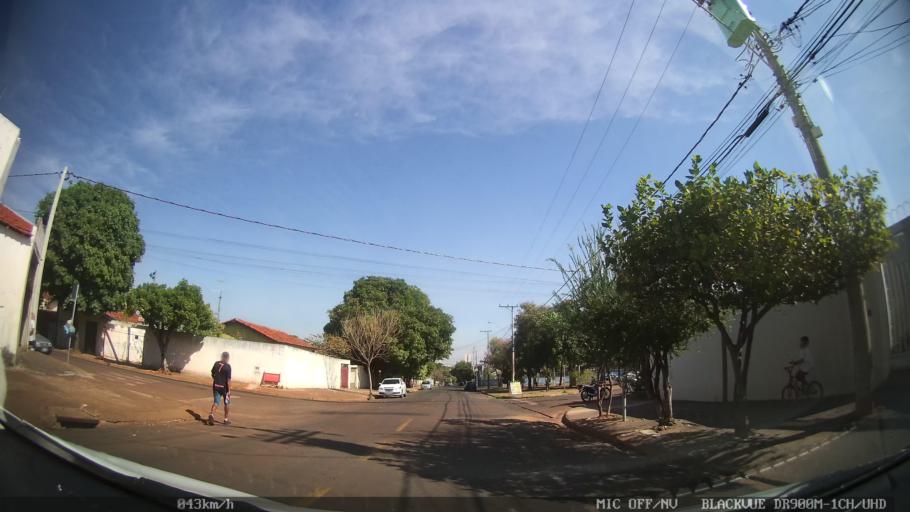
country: BR
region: Sao Paulo
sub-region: Sao Jose Do Rio Preto
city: Sao Jose do Rio Preto
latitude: -20.7882
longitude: -49.4032
